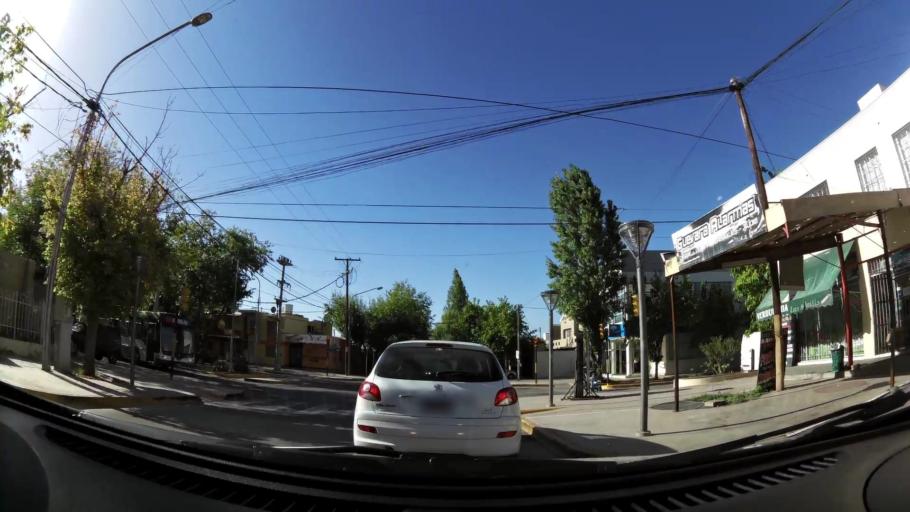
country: AR
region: Mendoza
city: Villa Nueva
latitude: -32.9098
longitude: -68.7969
